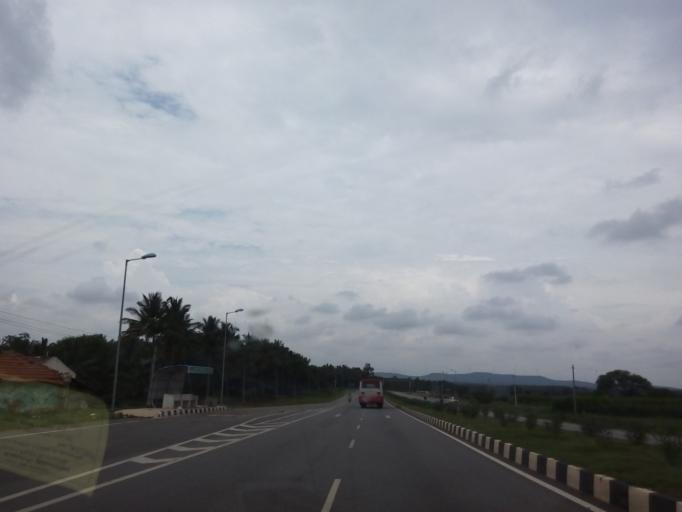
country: IN
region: Karnataka
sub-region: Hassan
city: Channarayapatna
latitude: 12.9419
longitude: 76.3531
